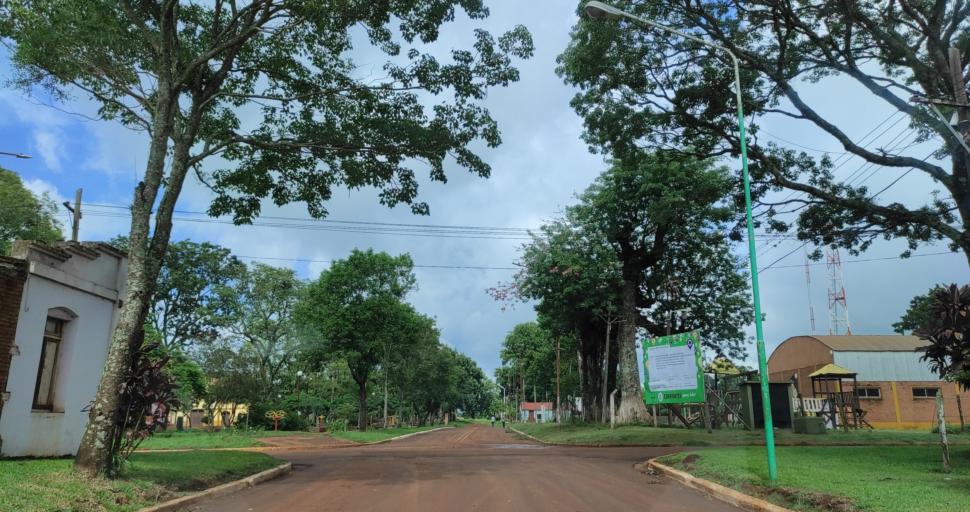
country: AR
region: Corrientes
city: San Carlos
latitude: -27.7430
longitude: -55.8977
